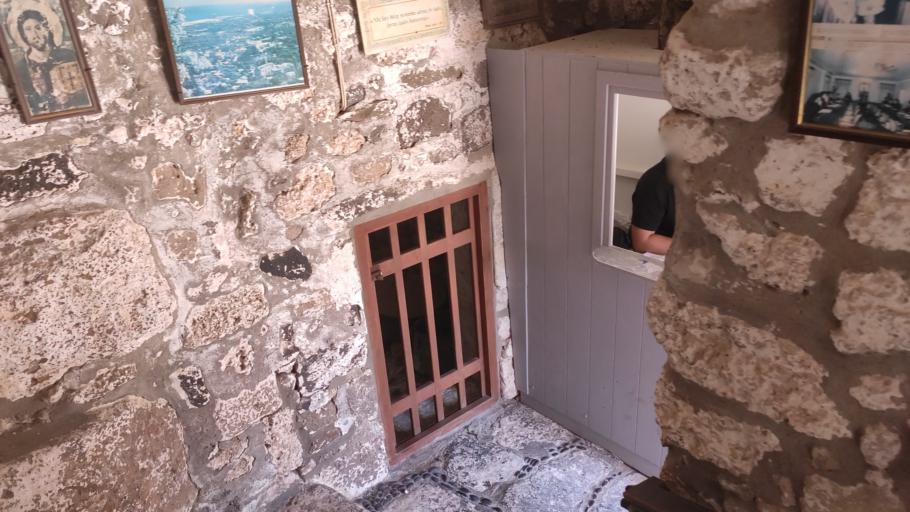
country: GR
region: South Aegean
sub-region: Nomos Dodekanisou
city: Mandraki
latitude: 36.6106
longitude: 27.1312
